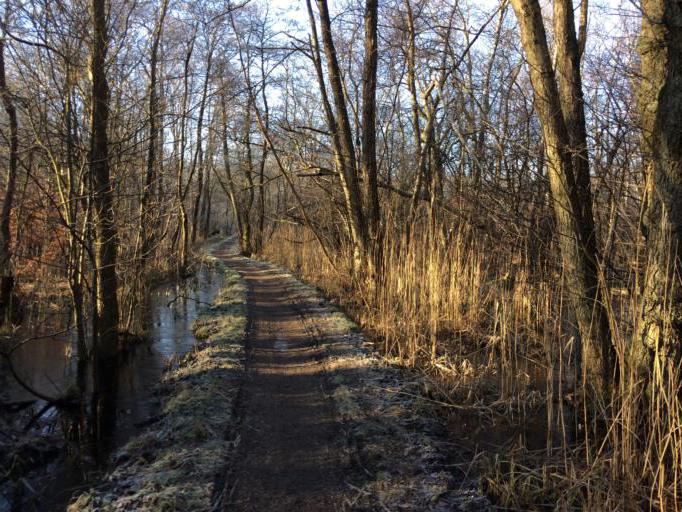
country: DK
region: Capital Region
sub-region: Gladsaxe Municipality
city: Buddinge
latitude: 55.7788
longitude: 12.4652
